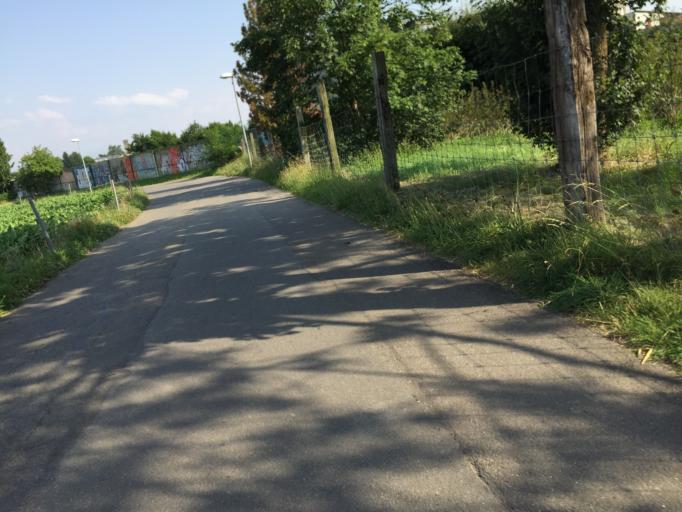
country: CH
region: Bern
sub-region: Bern-Mittelland District
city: Muri
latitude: 46.9367
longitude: 7.4925
